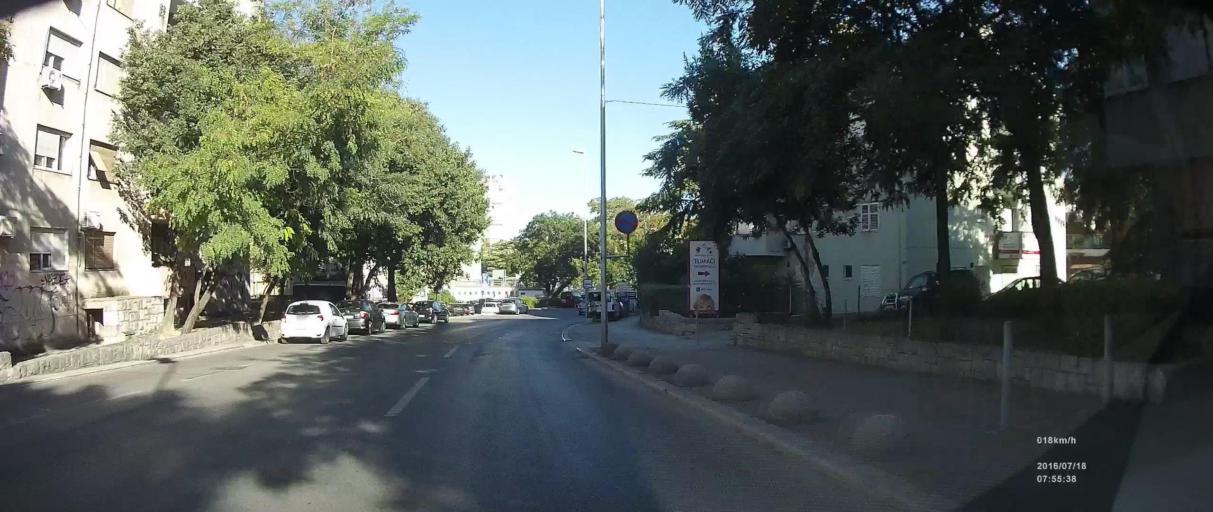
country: HR
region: Splitsko-Dalmatinska
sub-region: Grad Split
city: Split
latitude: 43.5136
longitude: 16.4455
